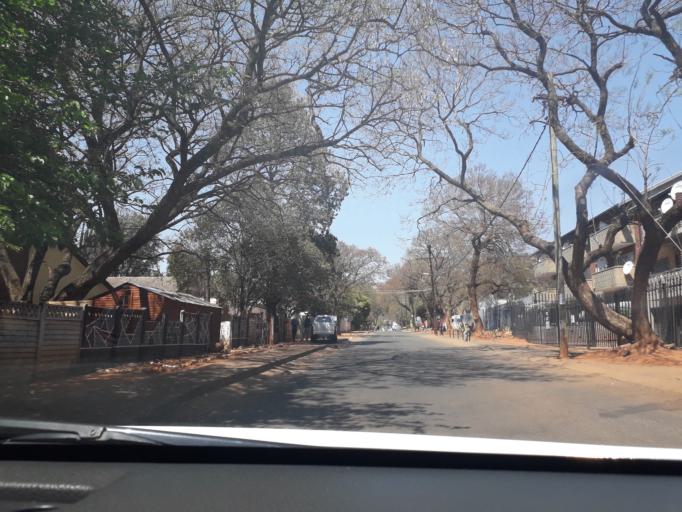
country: ZA
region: Gauteng
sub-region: City of Johannesburg Metropolitan Municipality
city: Roodepoort
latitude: -26.1225
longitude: 27.9659
